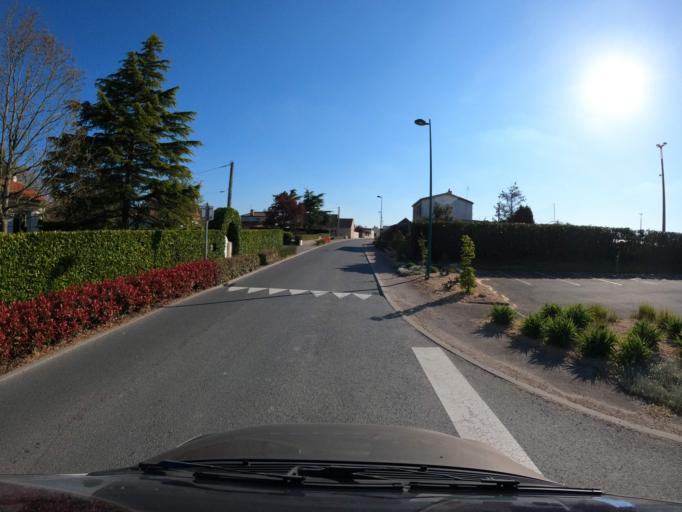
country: FR
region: Pays de la Loire
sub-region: Departement de la Vendee
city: Beaurepaire
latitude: 46.9096
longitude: -1.1304
